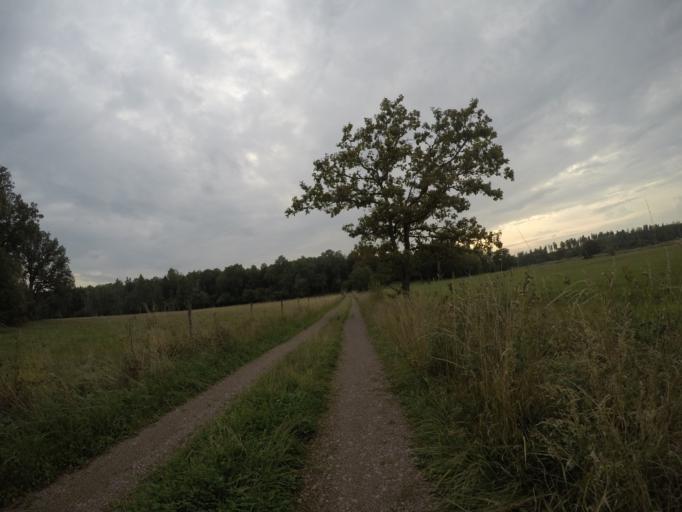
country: SE
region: Vaestmanland
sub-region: Hallstahammars Kommun
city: Kolback
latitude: 59.4809
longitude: 16.2141
